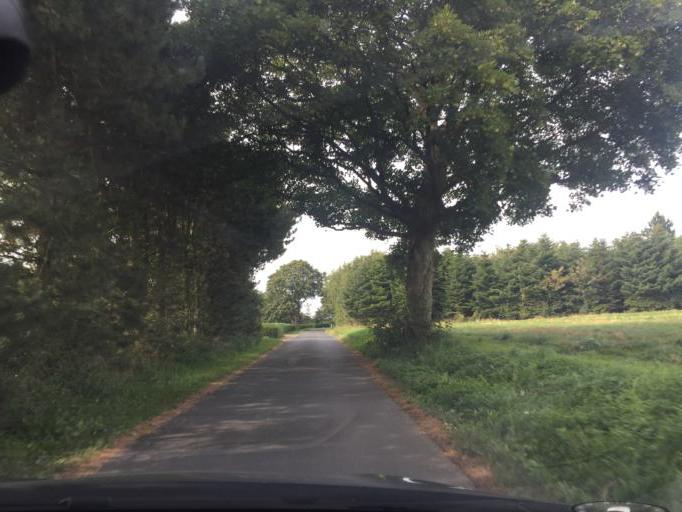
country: DK
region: South Denmark
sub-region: Faaborg-Midtfyn Kommune
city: Arslev
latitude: 55.3424
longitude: 10.5124
